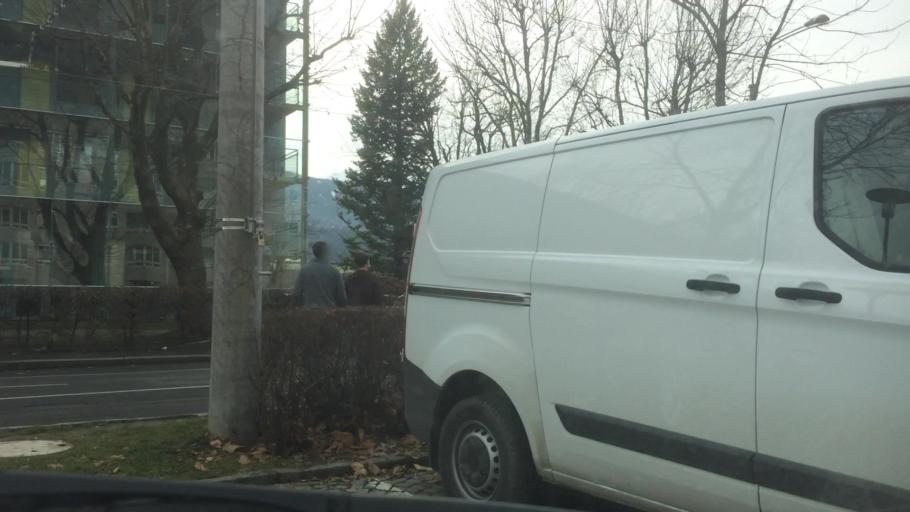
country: AT
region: Tyrol
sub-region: Politischer Bezirk Innsbruck Land
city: Vols
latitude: 47.2654
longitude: 11.3451
